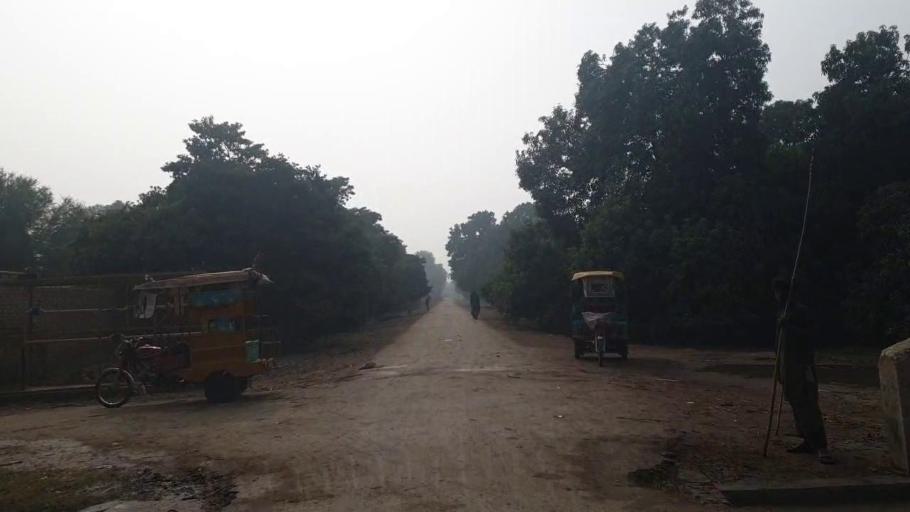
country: PK
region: Sindh
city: Tando Adam
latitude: 25.7855
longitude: 68.5962
